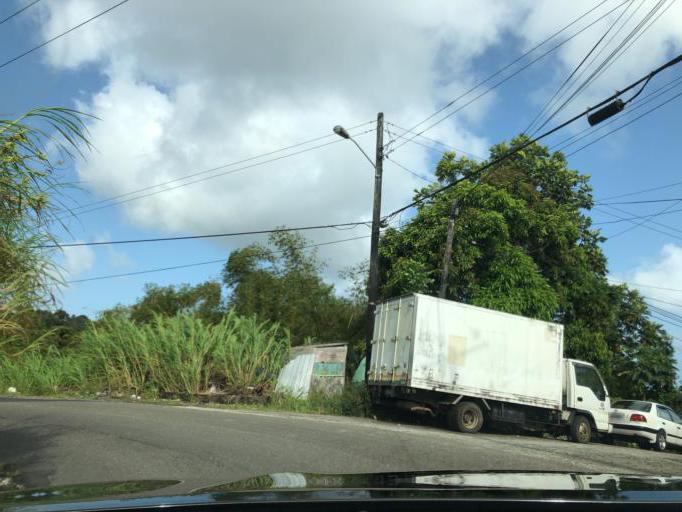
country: LC
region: Castries Quarter
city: Bisee
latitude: 13.9924
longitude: -60.9572
